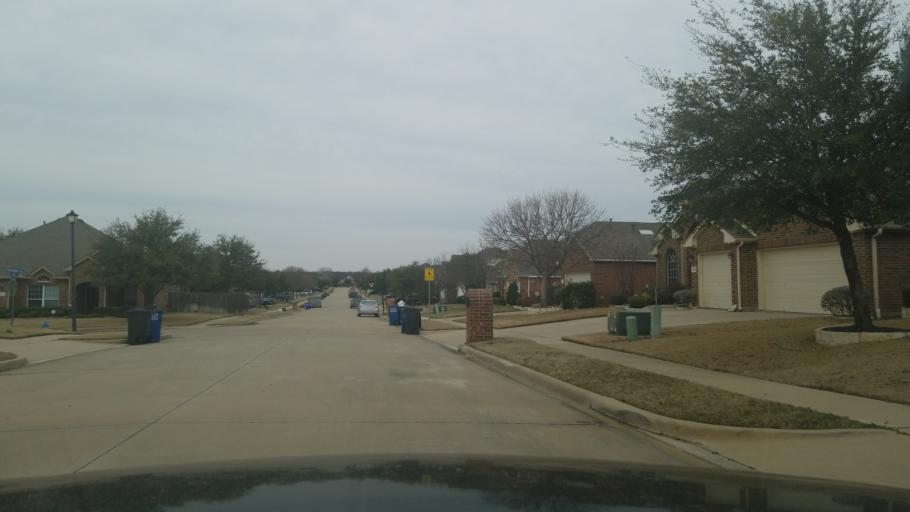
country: US
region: Texas
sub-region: Denton County
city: Corinth
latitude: 33.1311
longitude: -97.0727
